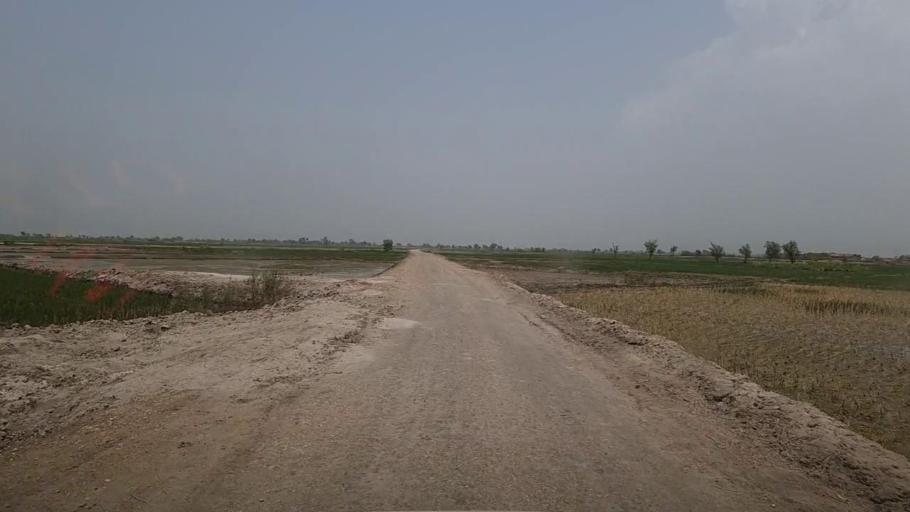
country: PK
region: Sindh
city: Sita Road
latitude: 27.0693
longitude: 67.8641
